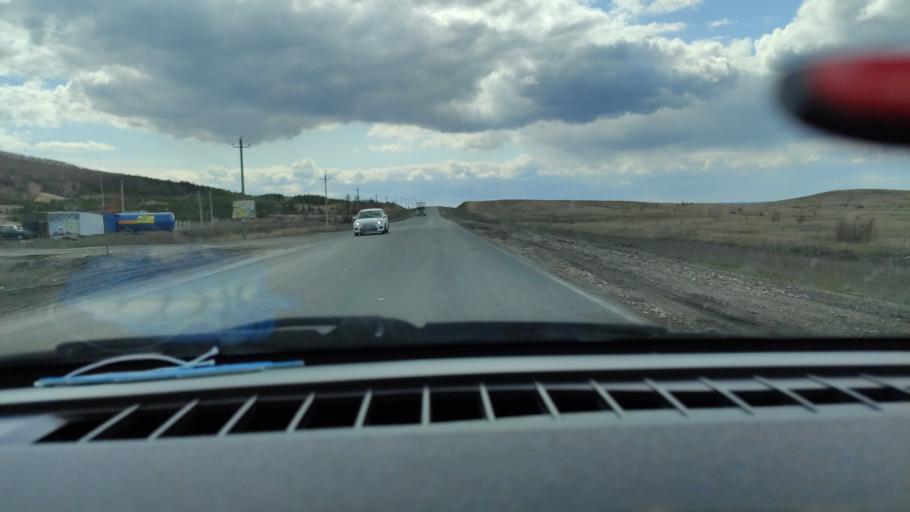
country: RU
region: Saratov
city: Alekseyevka
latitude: 52.3019
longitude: 47.9269
